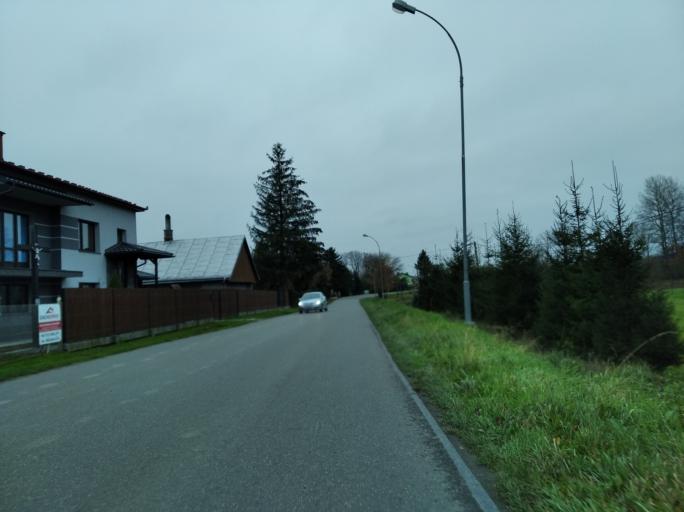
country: PL
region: Subcarpathian Voivodeship
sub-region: Powiat krosnienski
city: Jedlicze
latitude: 49.6954
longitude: 21.6577
